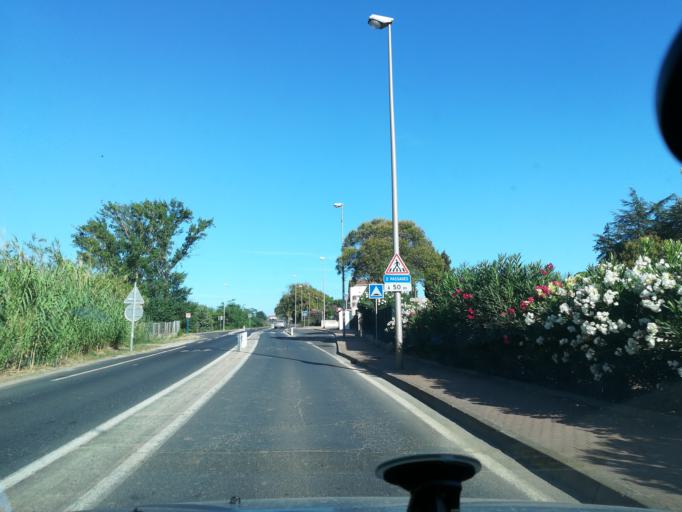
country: FR
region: Languedoc-Roussillon
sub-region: Departement de l'Herault
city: Portiragnes
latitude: 43.3052
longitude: 3.3292
